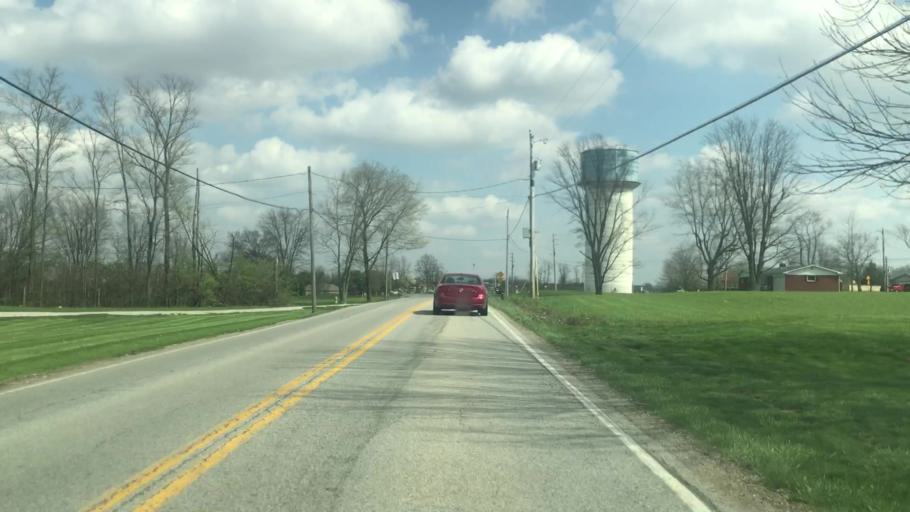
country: US
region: Indiana
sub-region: Johnson County
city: Waterloo
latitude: 39.5489
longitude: -86.2054
